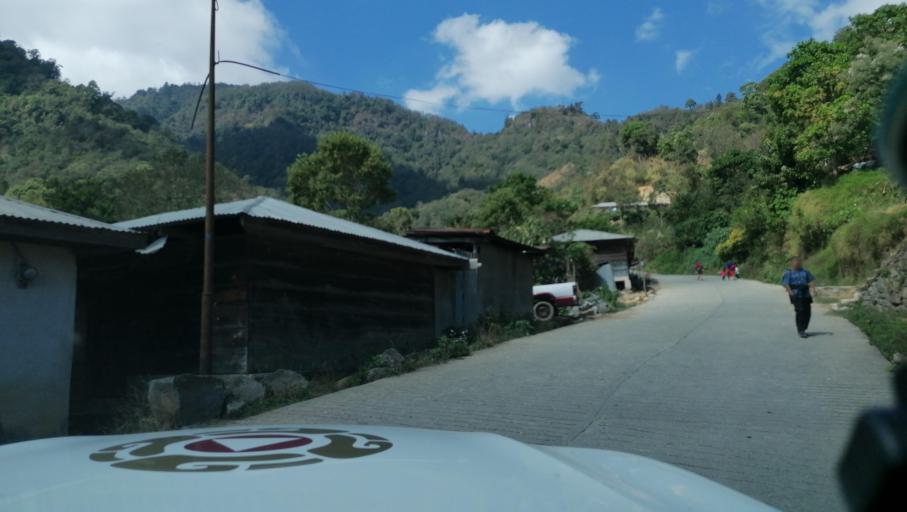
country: GT
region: San Marcos
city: Tacana
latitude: 15.2016
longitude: -92.2050
